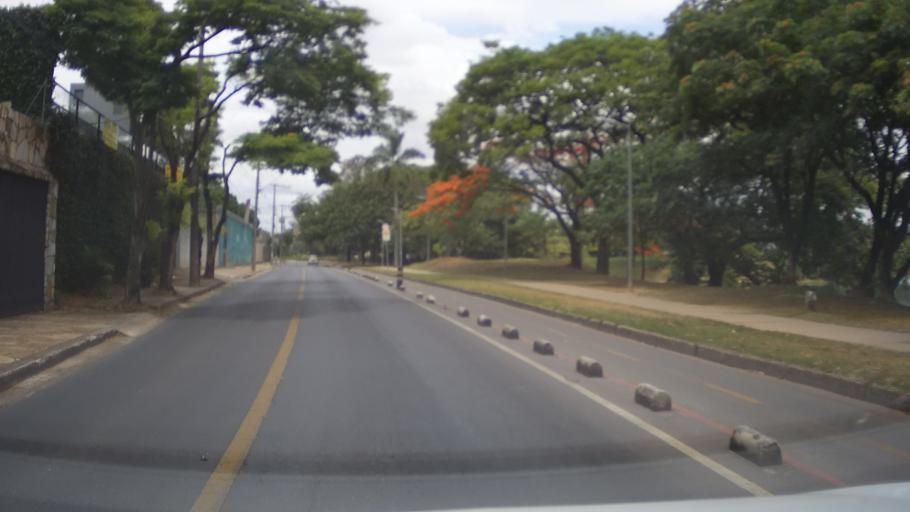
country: BR
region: Minas Gerais
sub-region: Belo Horizonte
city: Belo Horizonte
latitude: -19.8498
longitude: -43.9742
